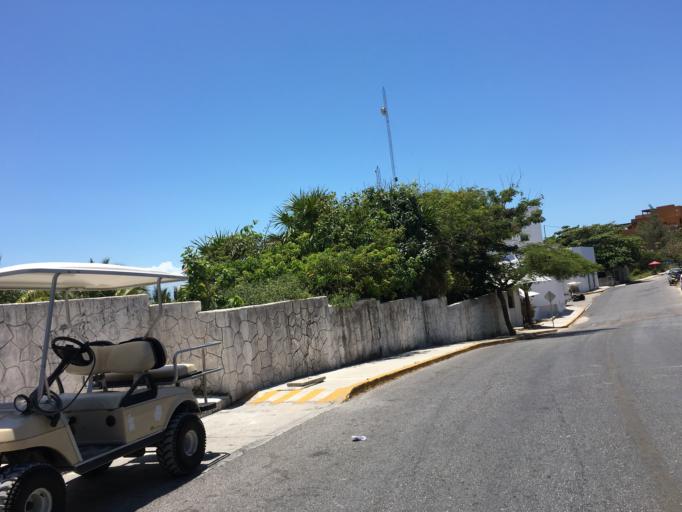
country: MX
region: Quintana Roo
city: Isla Mujeres
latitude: 21.2059
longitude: -86.7169
